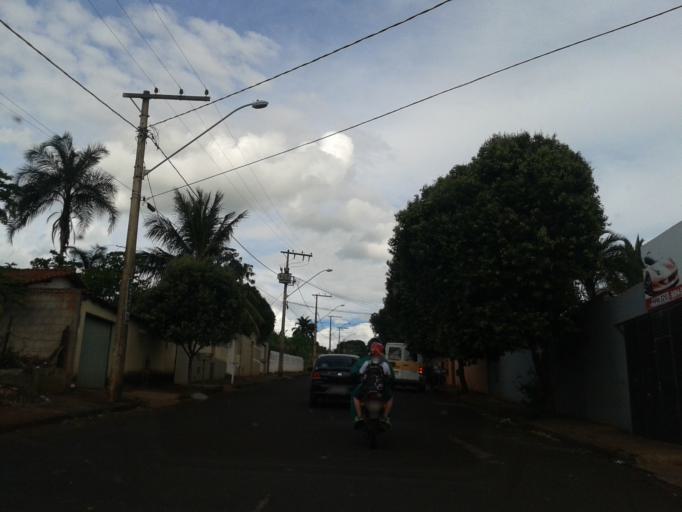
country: BR
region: Minas Gerais
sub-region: Ituiutaba
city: Ituiutaba
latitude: -18.9764
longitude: -49.4448
